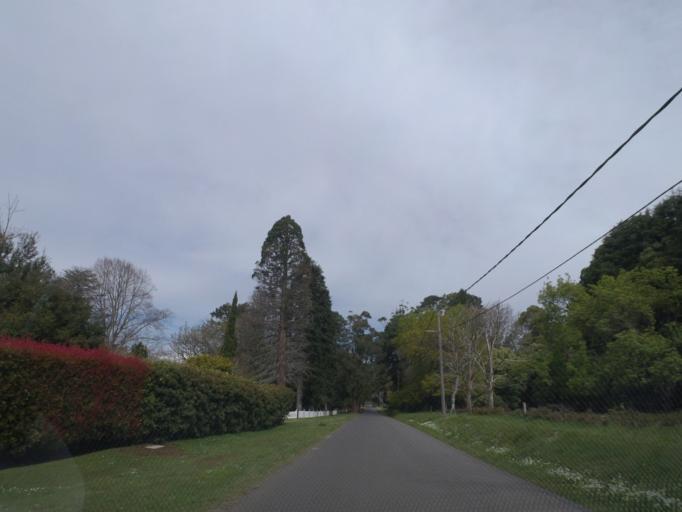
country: AU
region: Victoria
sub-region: Yarra Ranges
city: Mount Dandenong
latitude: -37.8266
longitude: 145.3643
